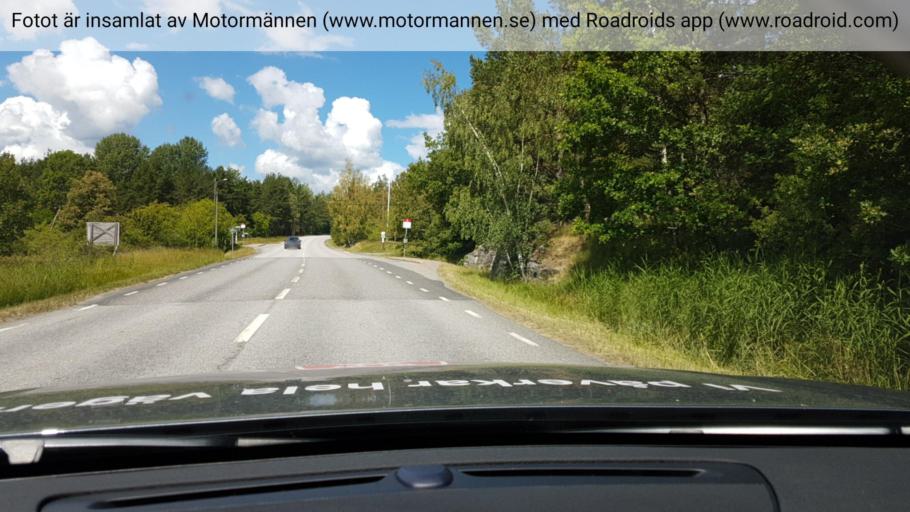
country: SE
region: Stockholm
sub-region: Varmdo Kommun
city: Hemmesta
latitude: 59.3397
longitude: 18.4855
